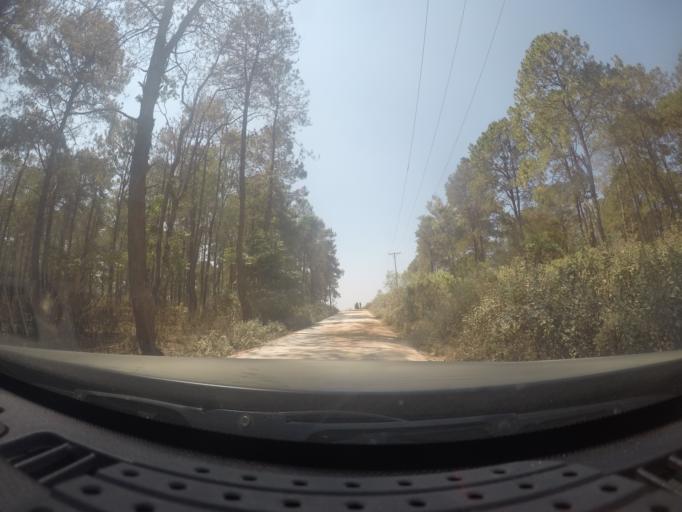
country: MM
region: Shan
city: Taunggyi
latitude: 20.9806
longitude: 96.5379
